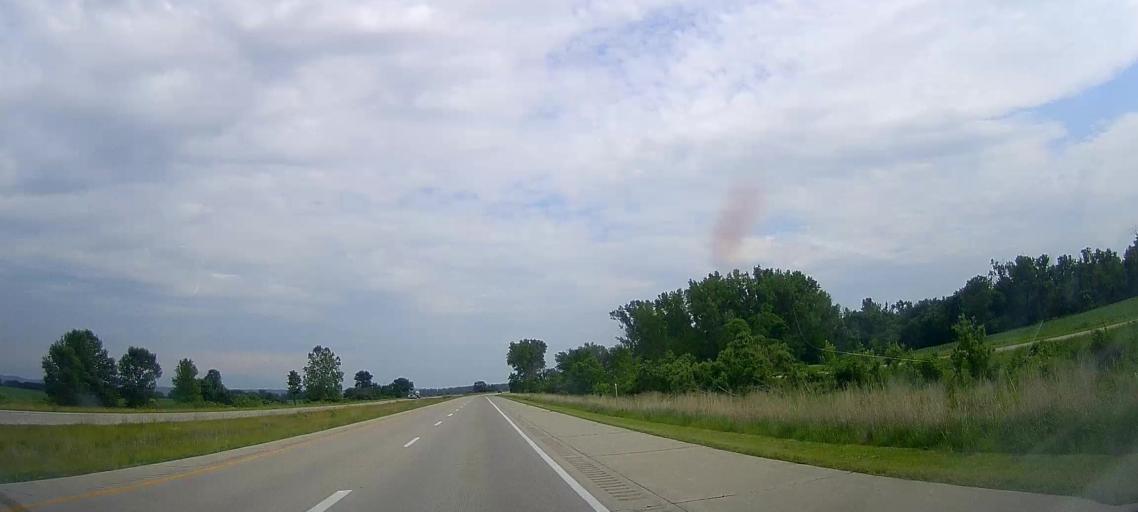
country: US
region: Nebraska
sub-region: Burt County
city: Tekamah
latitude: 41.8412
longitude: -96.0897
